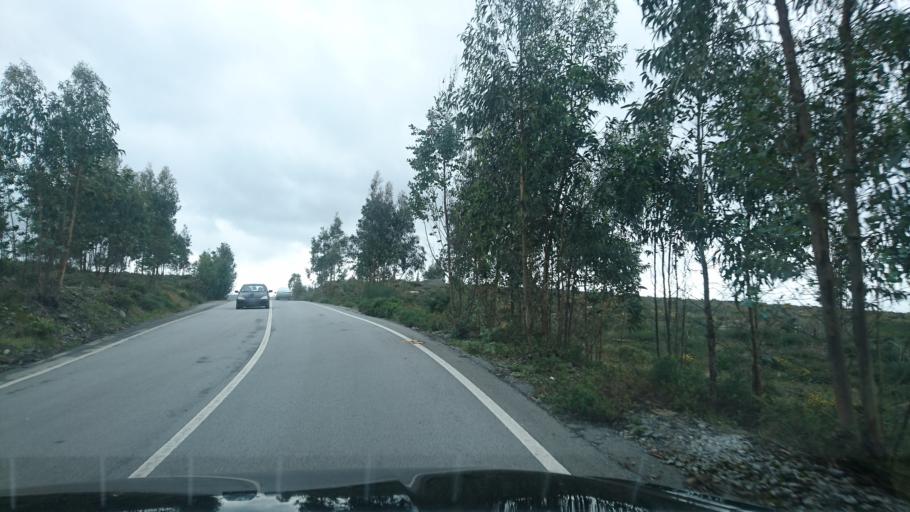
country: PT
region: Porto
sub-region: Paredes
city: Recarei
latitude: 41.1309
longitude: -8.4024
